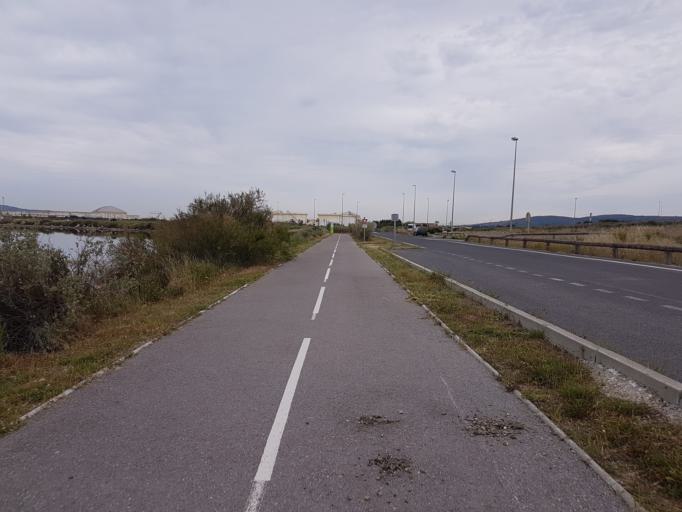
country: FR
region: Languedoc-Roussillon
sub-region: Departement de l'Herault
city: Frontignan
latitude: 43.4358
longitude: 3.7641
